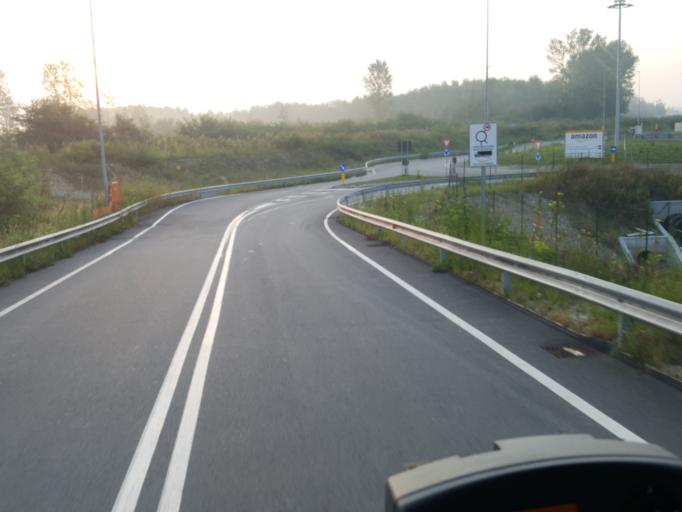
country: IT
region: Piedmont
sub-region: Provincia di Torino
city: Rondissone
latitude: 45.2359
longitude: 7.9764
